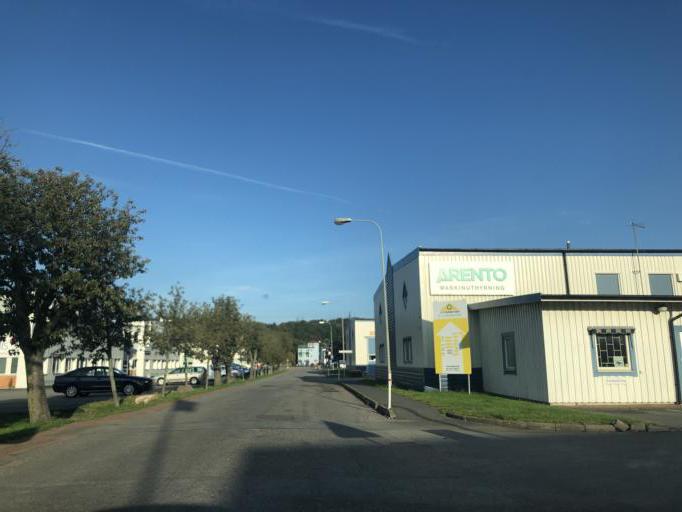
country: SE
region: Vaestra Goetaland
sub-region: Goteborg
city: Goeteborg
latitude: 57.7468
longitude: 11.9973
